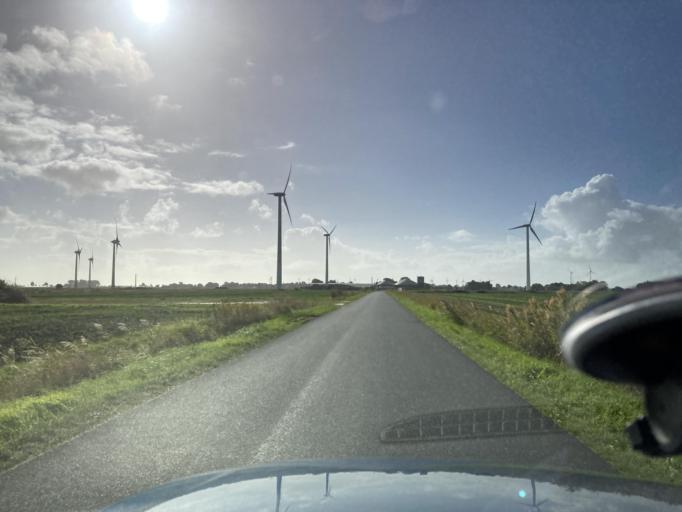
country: DE
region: Schleswig-Holstein
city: Norderwohrden
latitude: 54.1757
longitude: 9.0243
